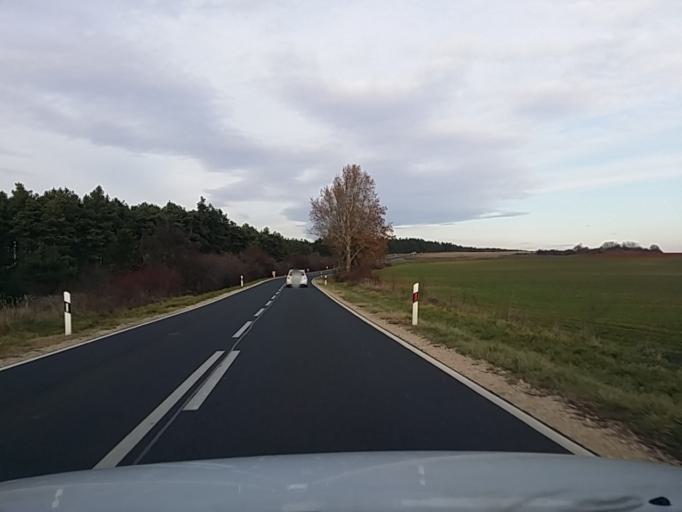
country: HU
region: Veszprem
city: Herend
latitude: 47.0060
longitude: 17.7486
